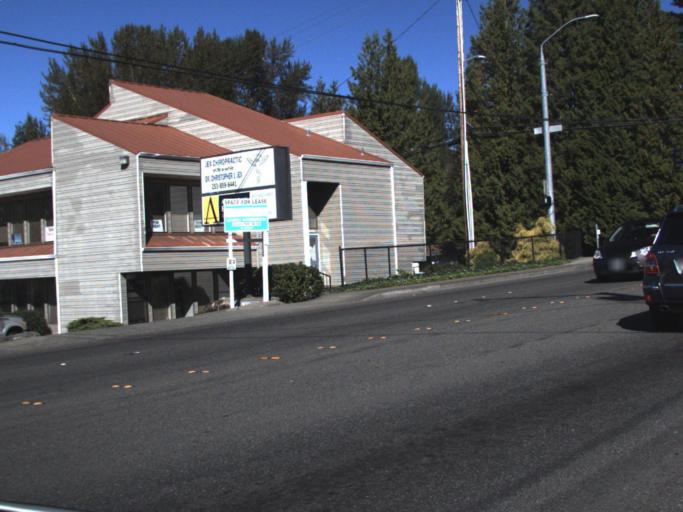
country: US
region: Washington
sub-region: King County
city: East Hill-Meridian
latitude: 47.4299
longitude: -122.1971
